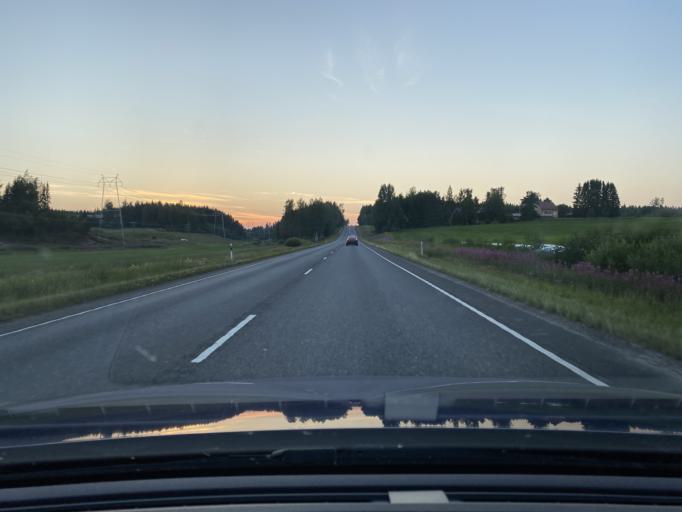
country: FI
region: Pirkanmaa
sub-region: Luoteis-Pirkanmaa
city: Ikaalinen
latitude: 61.8135
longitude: 22.9574
